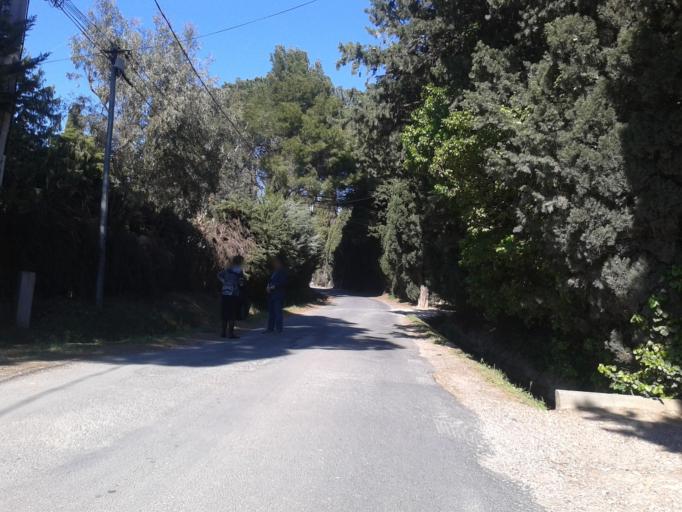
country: FR
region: Languedoc-Roussillon
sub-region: Departement des Pyrenees-Orientales
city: Pezilla-la-Riviere
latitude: 42.6988
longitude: 2.7706
